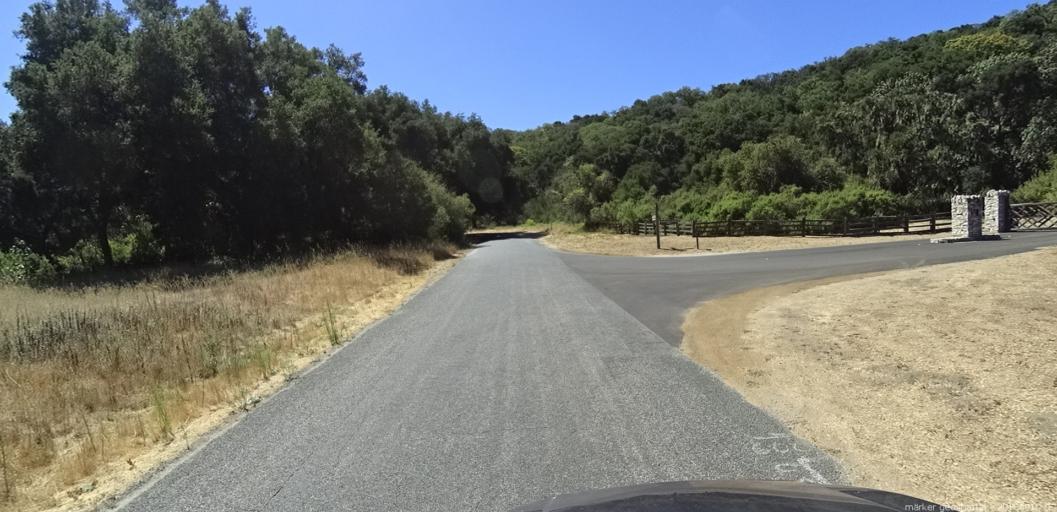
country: US
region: California
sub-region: Monterey County
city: Carmel Valley Village
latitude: 36.4434
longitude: -121.7965
